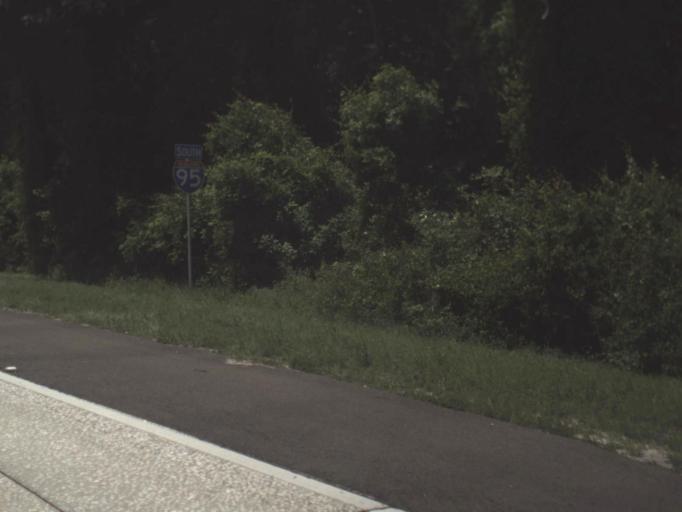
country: US
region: Florida
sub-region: Duval County
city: Jacksonville
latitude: 30.4520
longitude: -81.6518
